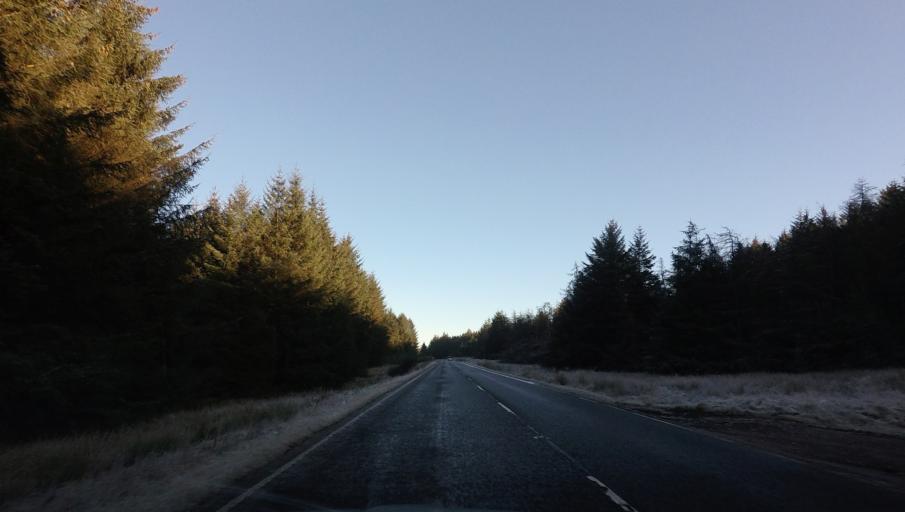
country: GB
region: Scotland
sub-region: West Lothian
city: Fauldhouse
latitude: 55.8123
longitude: -3.7093
